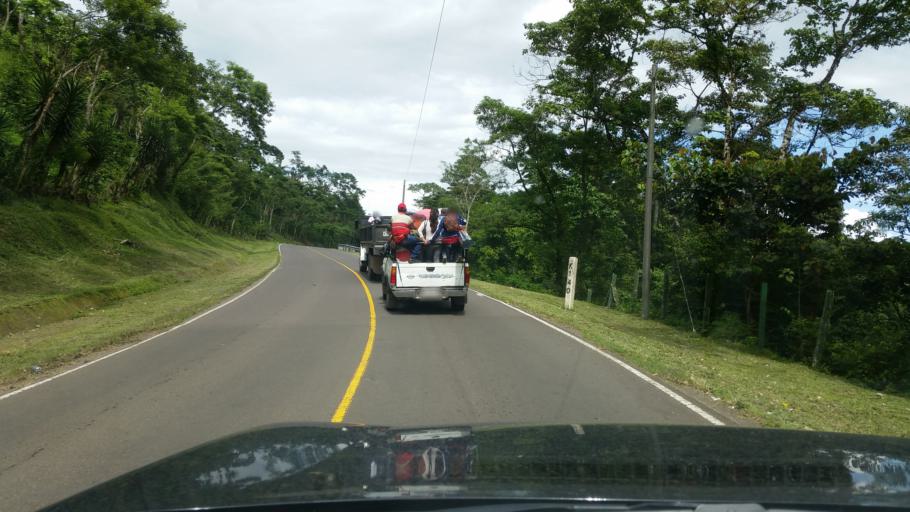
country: NI
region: Matagalpa
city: San Ramon
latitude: 12.9602
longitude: -85.8604
